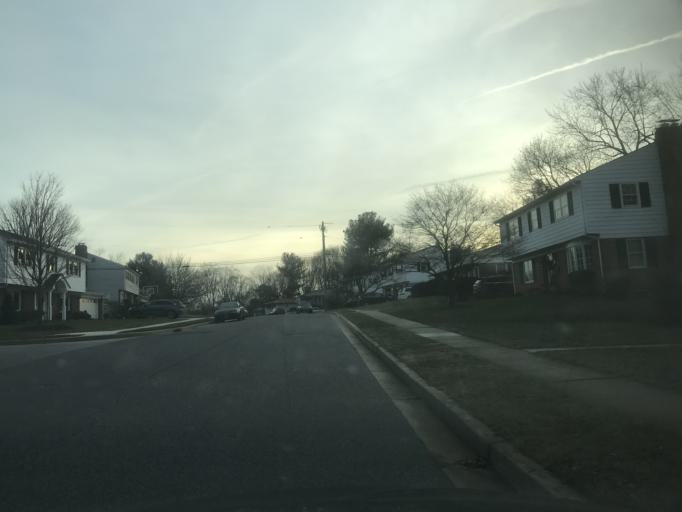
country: US
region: Maryland
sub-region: Baltimore County
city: Timonium
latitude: 39.4553
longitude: -76.6098
